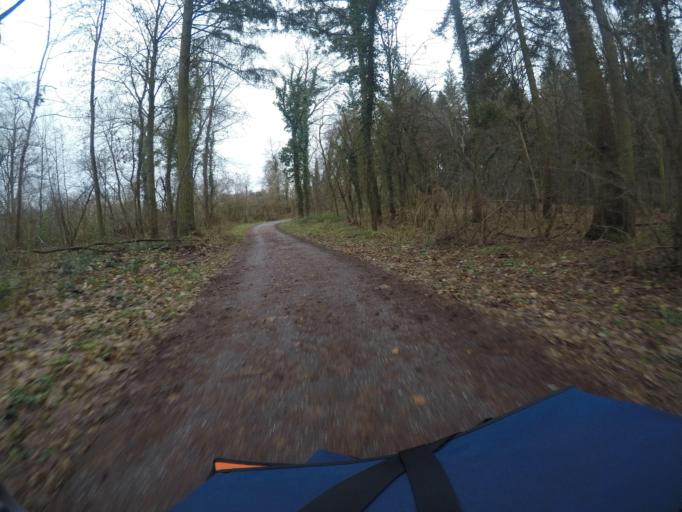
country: DE
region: Baden-Wuerttemberg
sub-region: Karlsruhe Region
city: Graben-Neudorf
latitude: 49.1921
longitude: 8.5049
